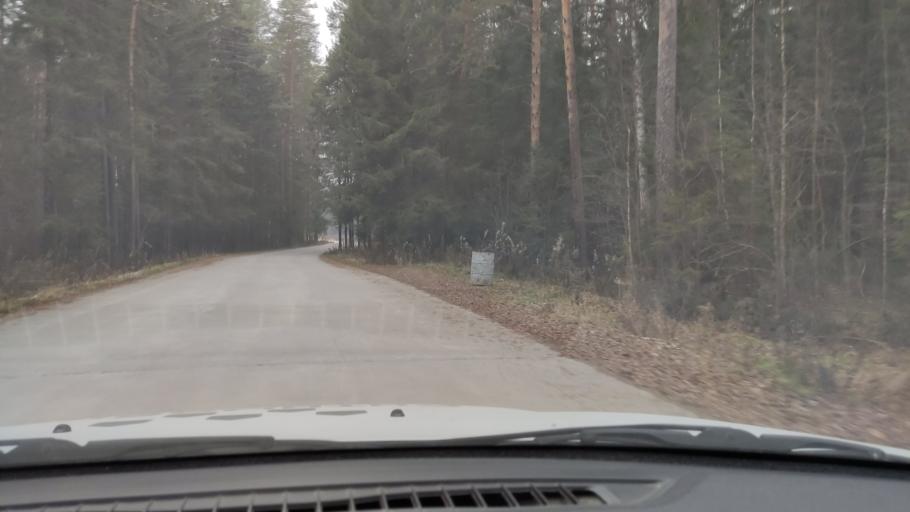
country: RU
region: Perm
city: Kondratovo
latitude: 58.0474
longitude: 56.1467
